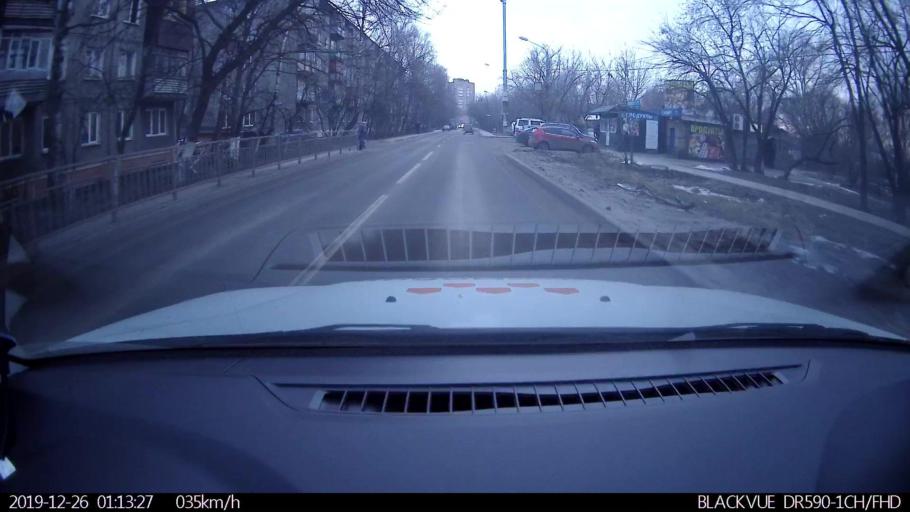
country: RU
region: Nizjnij Novgorod
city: Nizhniy Novgorod
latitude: 56.2781
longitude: 43.9110
